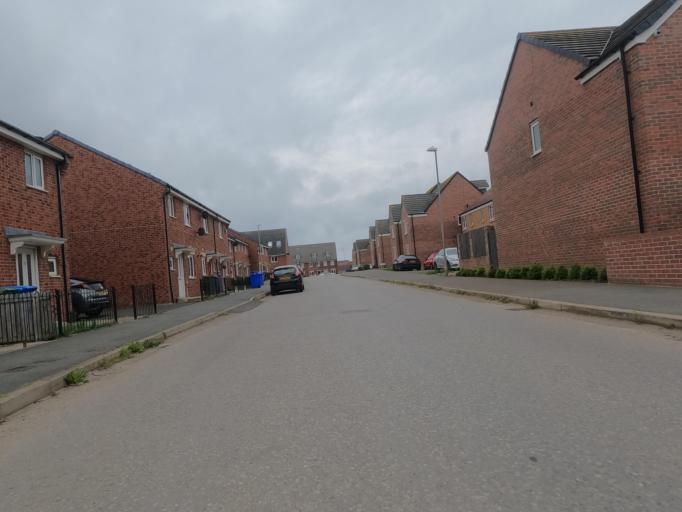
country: GB
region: England
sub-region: Northumberland
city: Blyth
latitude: 55.1206
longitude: -1.5447
